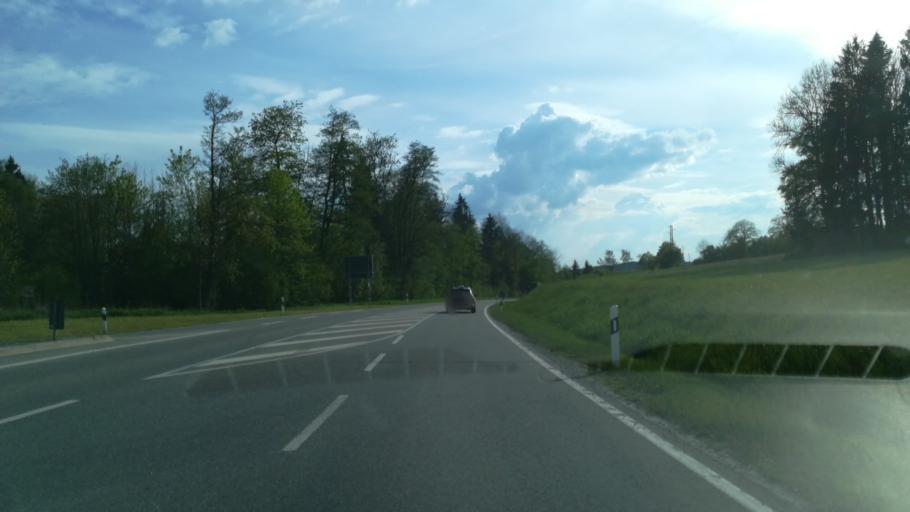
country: DE
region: Baden-Wuerttemberg
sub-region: Freiburg Region
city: Muhlingen
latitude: 47.9170
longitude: 9.0519
